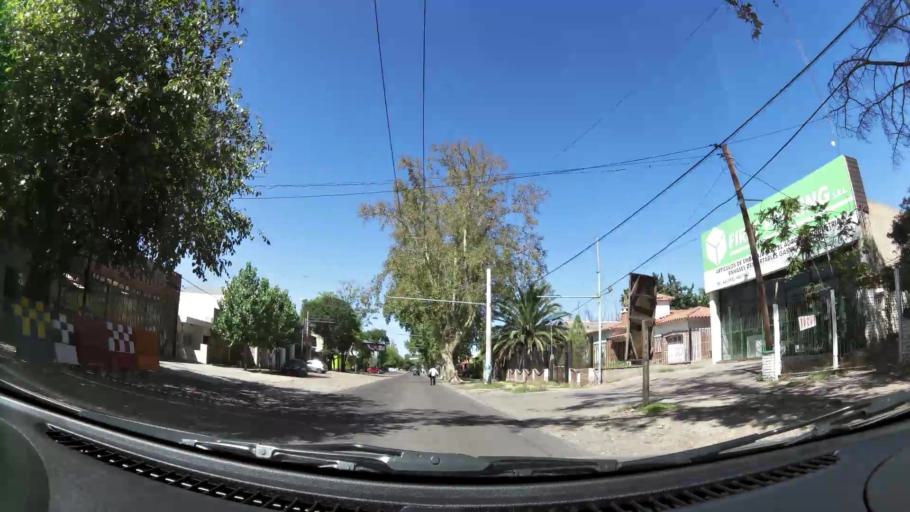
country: AR
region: Mendoza
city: Villa Nueva
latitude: -32.8925
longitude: -68.7999
